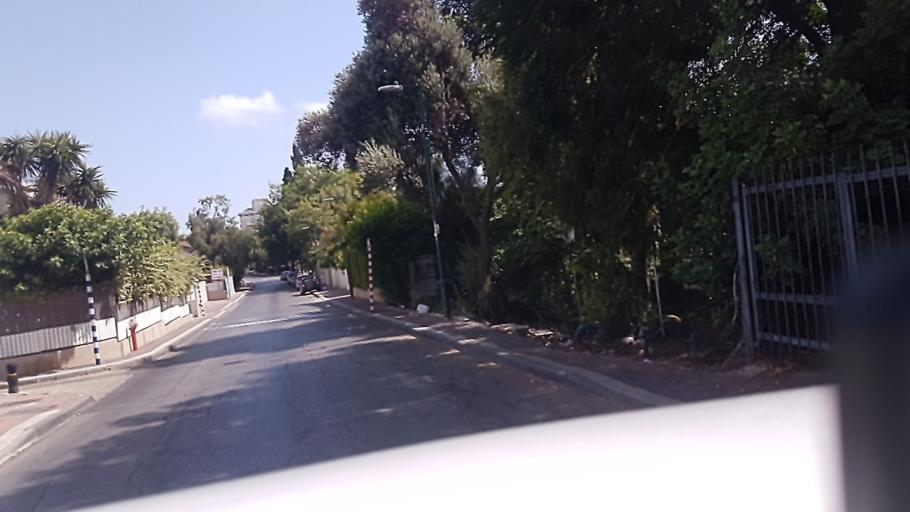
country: IL
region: Central District
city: Ganne Tiqwa
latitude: 32.0621
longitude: 34.8574
